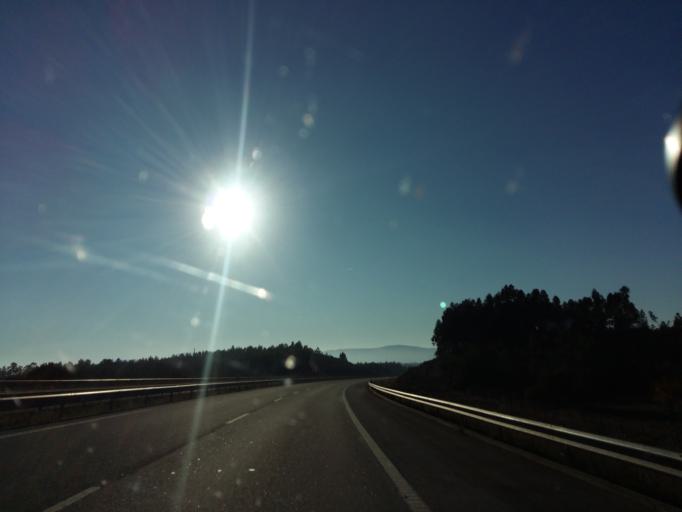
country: PT
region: Castelo Branco
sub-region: Castelo Branco
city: Castelo Branco
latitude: 39.7433
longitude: -7.6362
